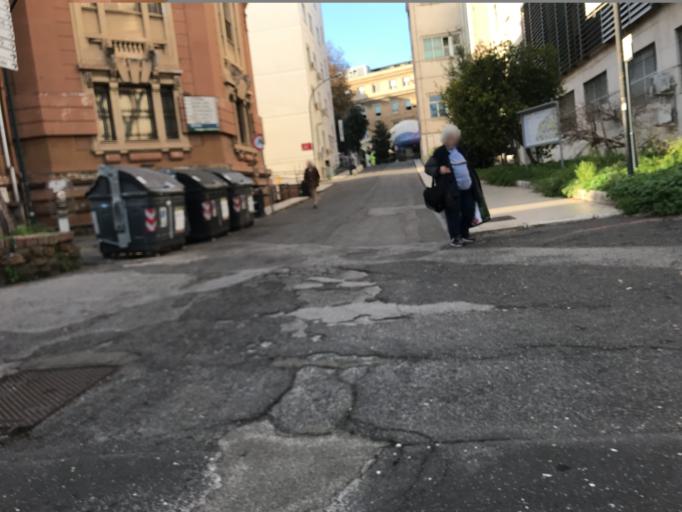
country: IT
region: Latium
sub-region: Citta metropolitana di Roma Capitale
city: Rome
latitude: 41.9073
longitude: 12.5134
